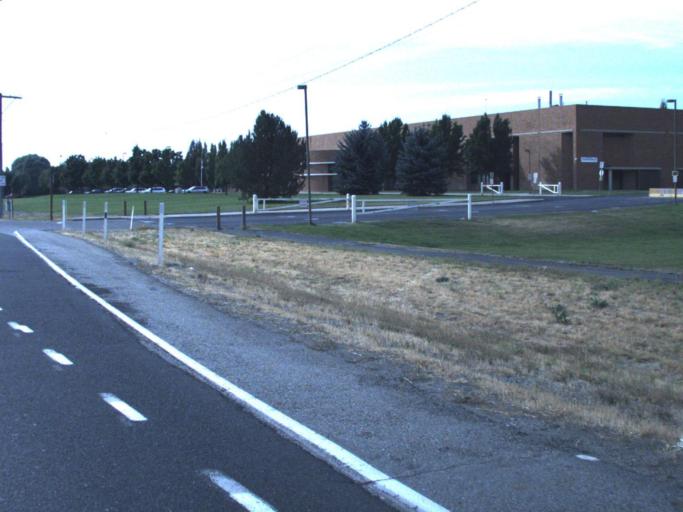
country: US
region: Washington
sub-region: Spokane County
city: Mead
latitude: 47.7874
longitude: -117.3206
